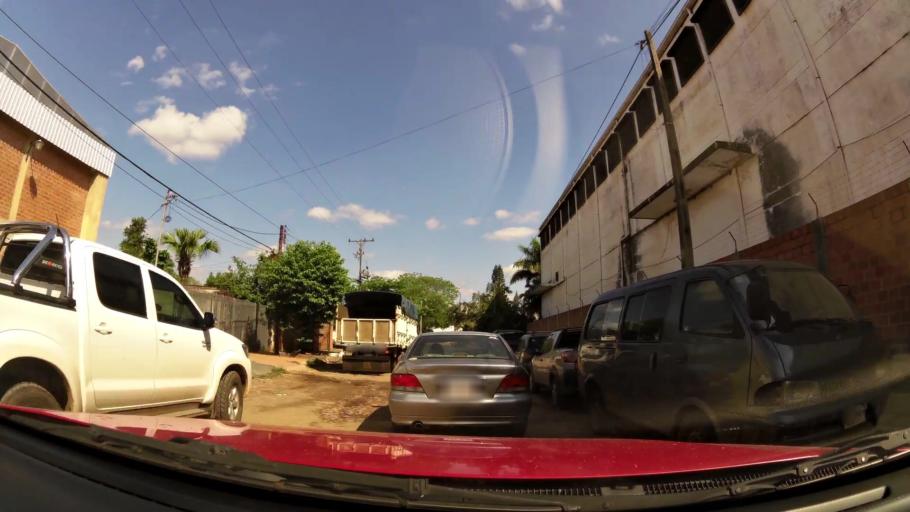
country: PY
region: Central
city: San Lorenzo
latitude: -25.3433
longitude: -57.4996
